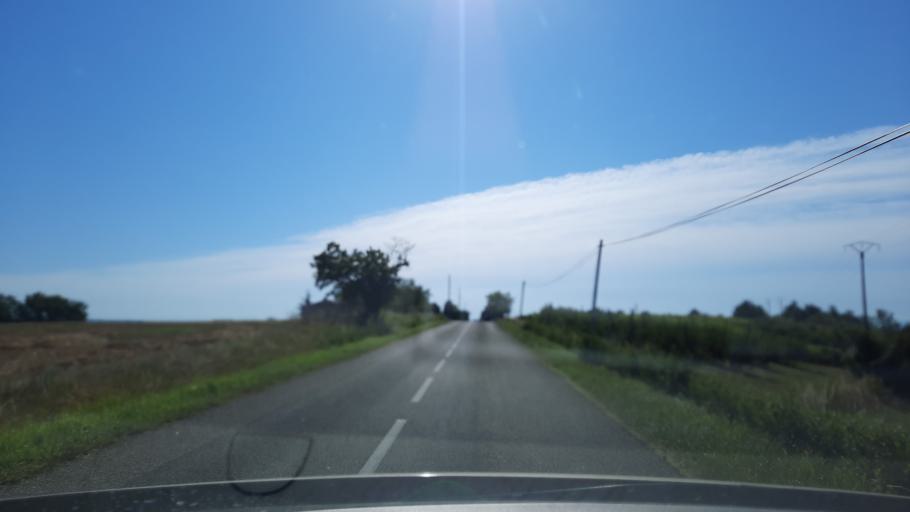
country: FR
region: Midi-Pyrenees
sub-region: Departement du Tarn-et-Garonne
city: Molieres
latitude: 44.2027
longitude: 1.4062
